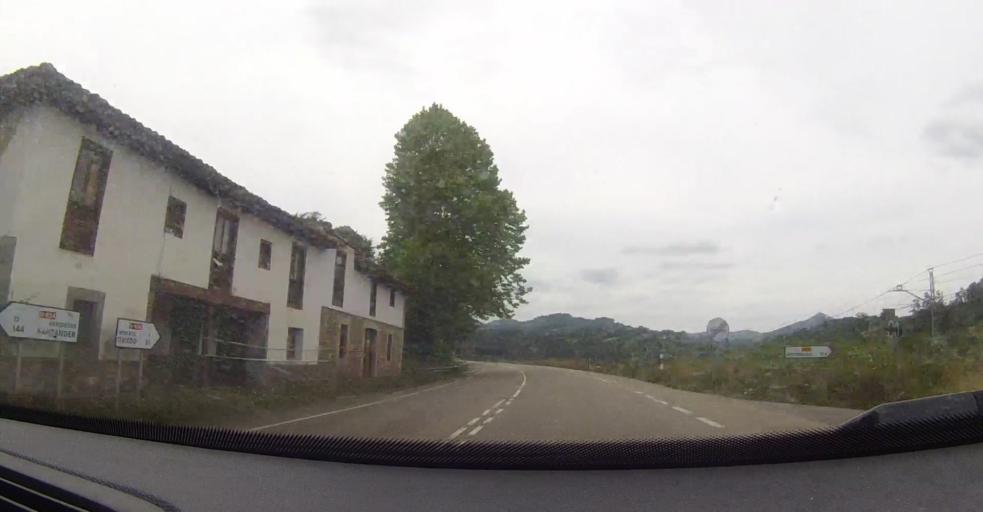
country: ES
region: Asturias
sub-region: Province of Asturias
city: Pilona
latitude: 43.3675
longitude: -5.2870
